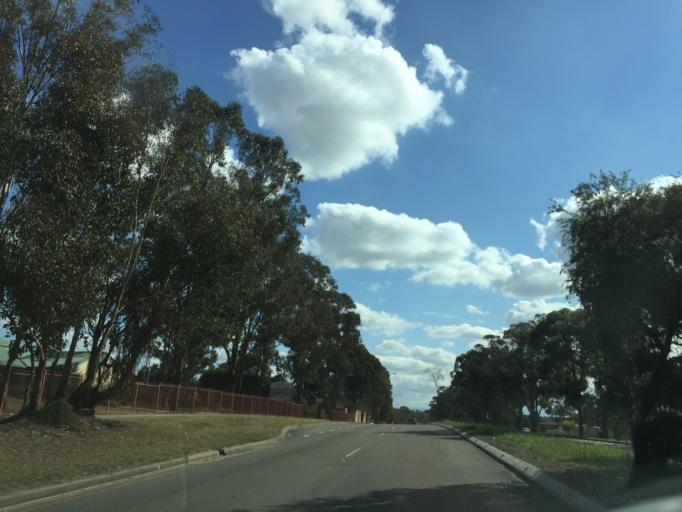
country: AU
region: New South Wales
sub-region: Blacktown
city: Quakers Hill
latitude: -33.7494
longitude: 150.8831
